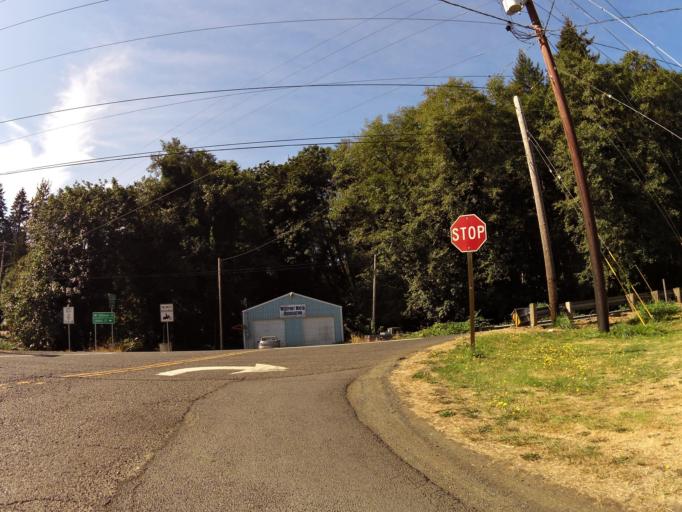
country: US
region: Washington
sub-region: Wahkiakum County
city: Cathlamet
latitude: 46.1323
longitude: -123.3762
